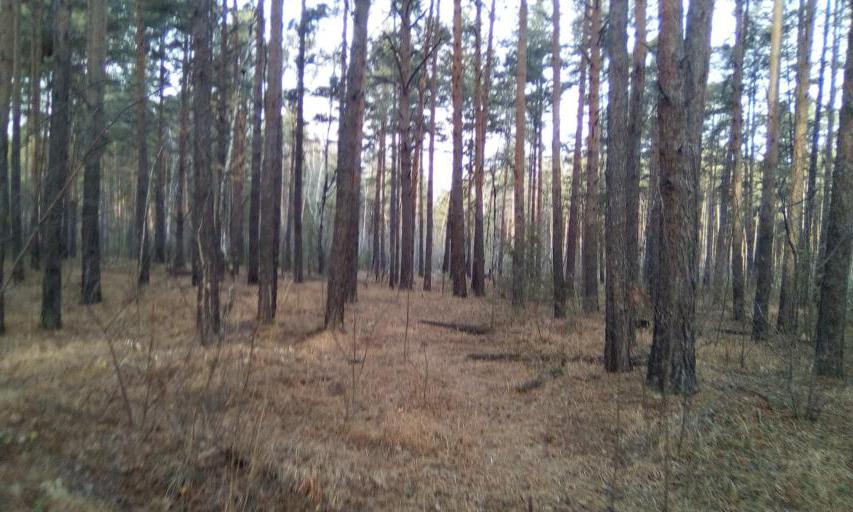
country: RU
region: Chelyabinsk
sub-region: Gorod Chelyabinsk
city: Chelyabinsk
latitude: 55.1622
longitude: 61.3519
